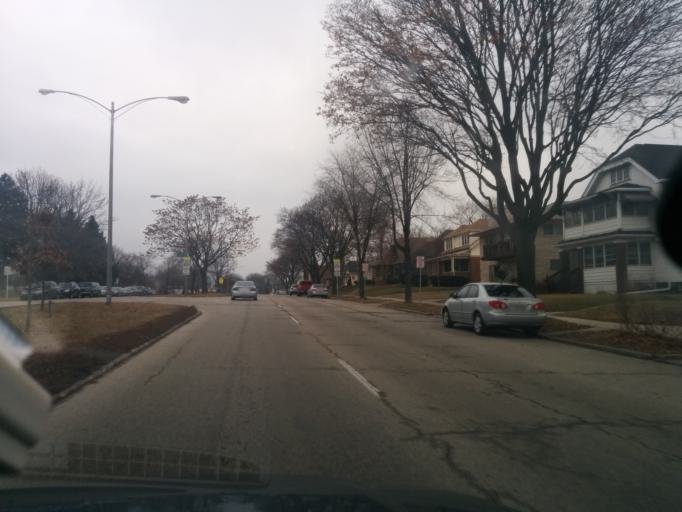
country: US
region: Wisconsin
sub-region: Milwaukee County
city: West Milwaukee
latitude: 43.0388
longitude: -87.9804
